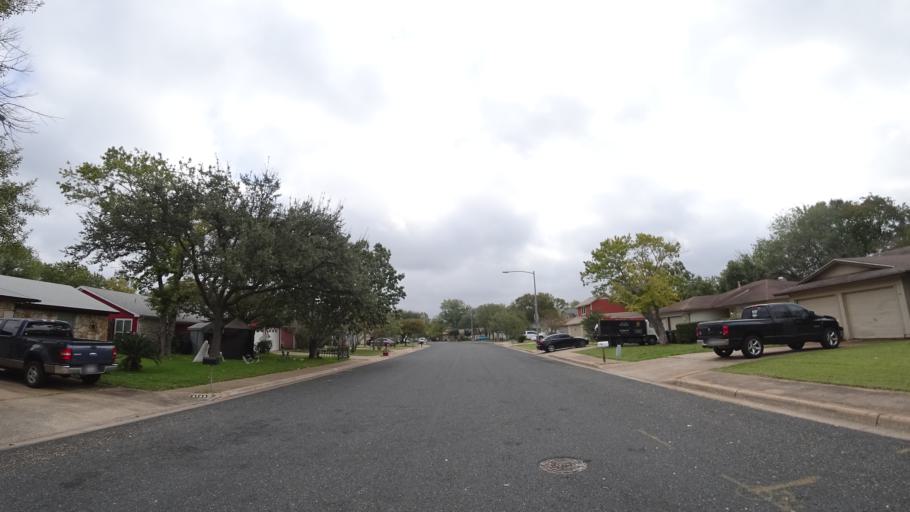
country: US
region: Texas
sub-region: Travis County
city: Shady Hollow
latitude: 30.2112
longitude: -97.8371
